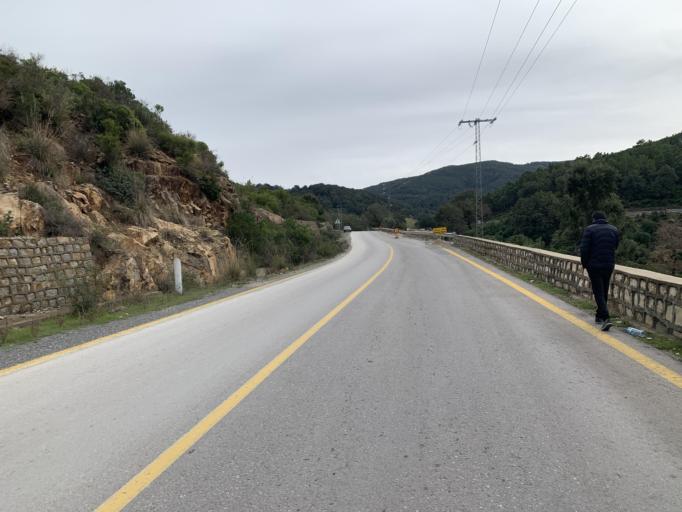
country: TN
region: Jundubah
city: Al Firnanah
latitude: 36.8037
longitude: 8.6519
